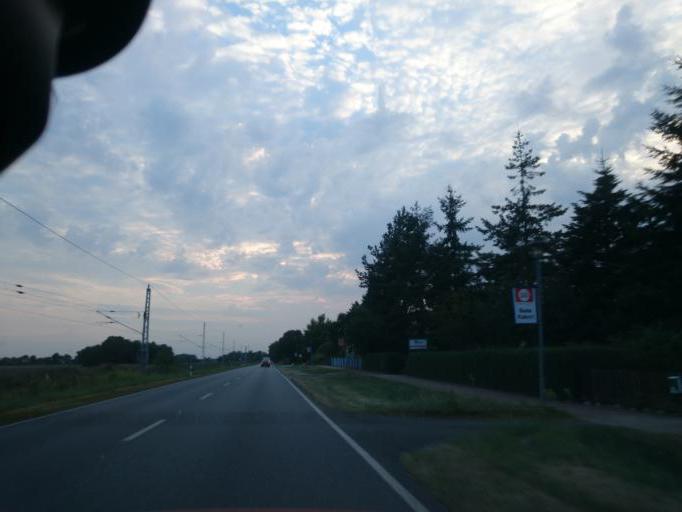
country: DE
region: Mecklenburg-Vorpommern
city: Rovershagen
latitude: 54.1808
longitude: 12.2585
